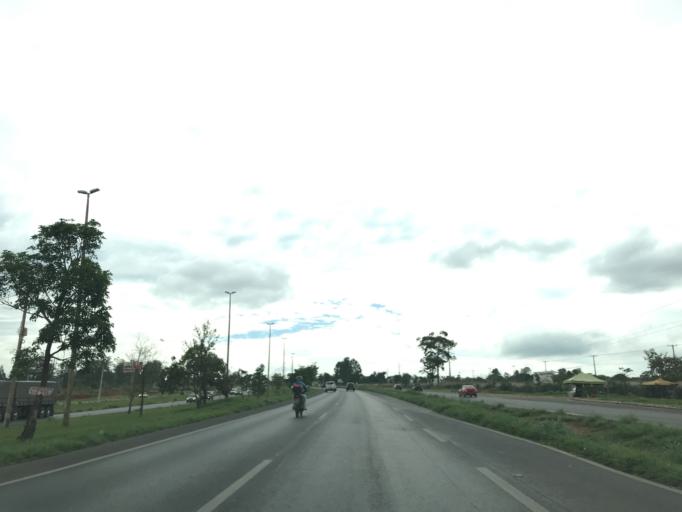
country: BR
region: Federal District
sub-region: Brasilia
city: Brasilia
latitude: -15.6670
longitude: -47.8108
